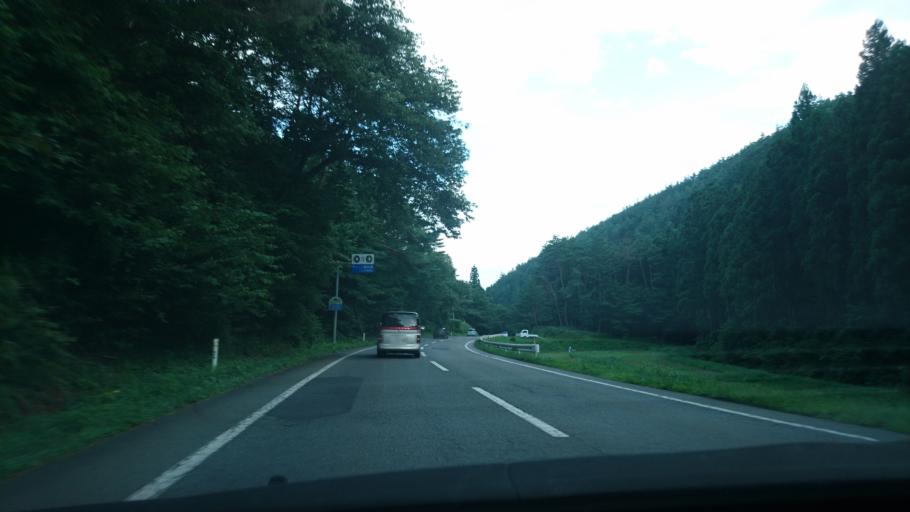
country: JP
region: Iwate
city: Mizusawa
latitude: 39.0480
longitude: 141.2326
